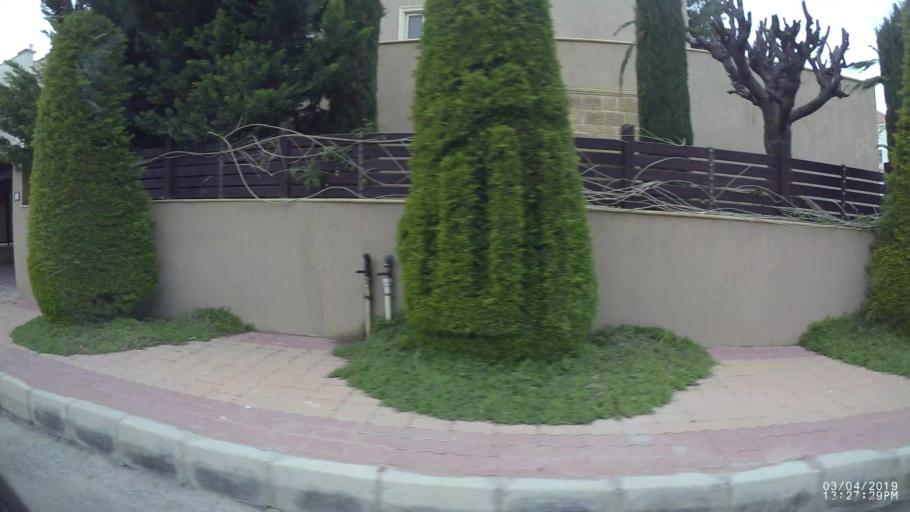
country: JO
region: Amman
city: Wadi as Sir
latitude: 31.9636
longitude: 35.8207
